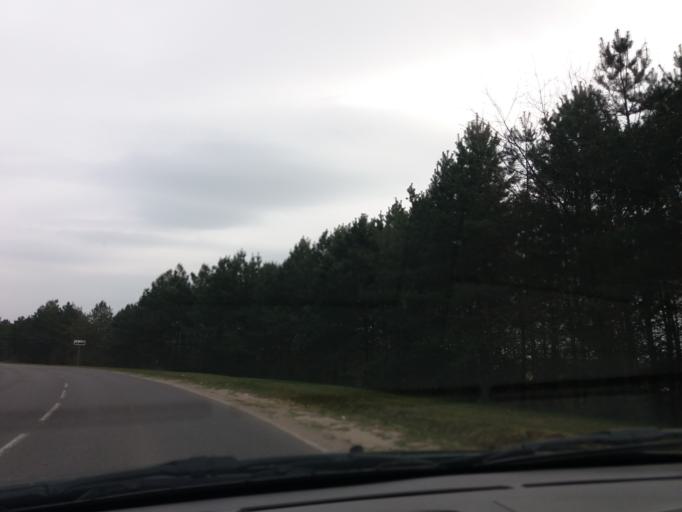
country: PL
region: Masovian Voivodeship
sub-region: Powiat mlawski
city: Mlawa
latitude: 53.1293
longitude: 20.3800
